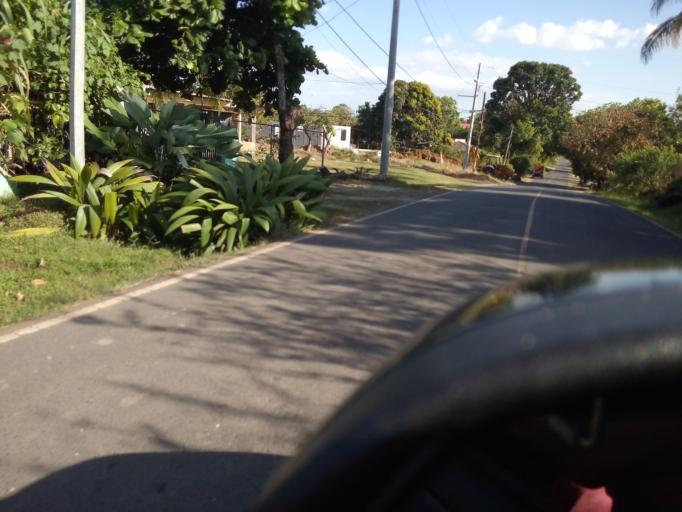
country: PA
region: Veraguas
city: Atalaya
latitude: 8.0426
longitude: -80.9264
